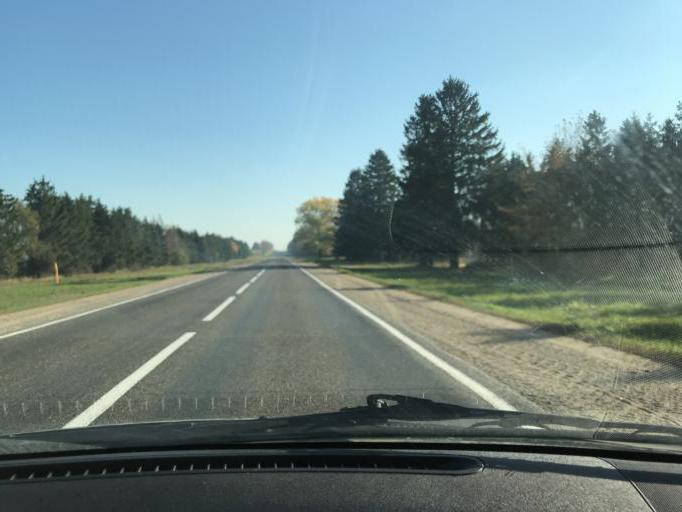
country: BY
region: Minsk
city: Klyetsk
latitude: 52.9662
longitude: 26.5472
